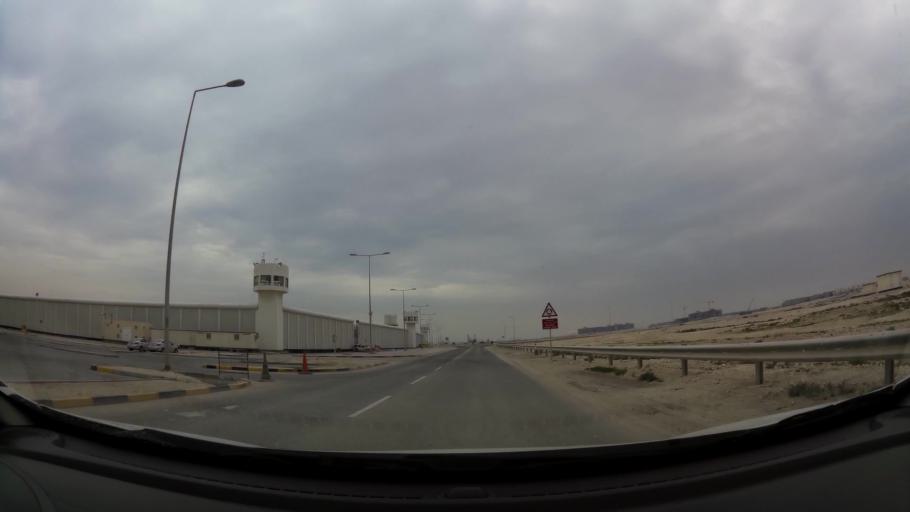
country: BH
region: Central Governorate
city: Dar Kulayb
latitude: 25.9949
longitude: 50.6162
